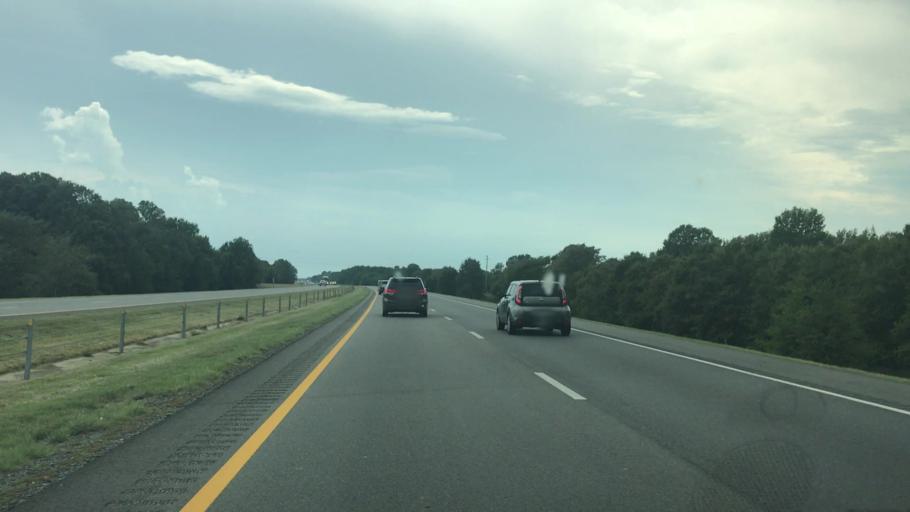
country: US
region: Arkansas
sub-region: Monroe County
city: Brinkley
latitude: 34.8996
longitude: -91.2398
